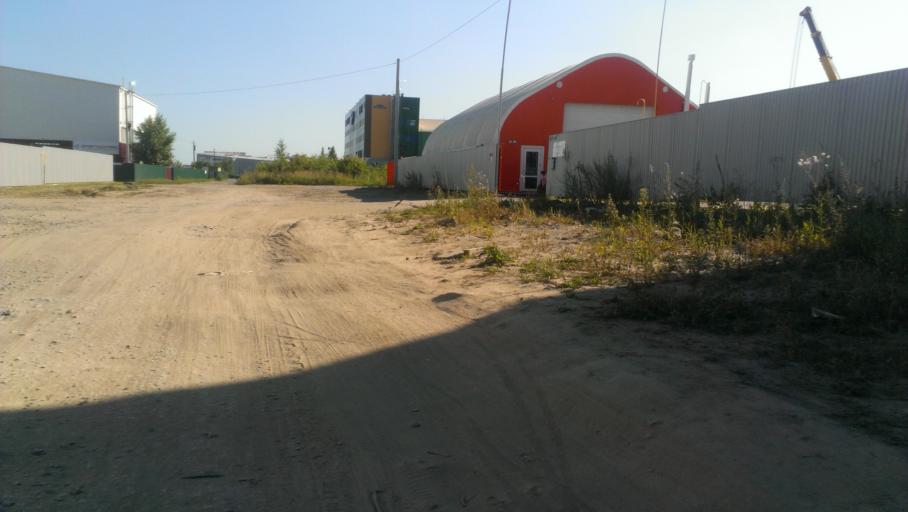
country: RU
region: Altai Krai
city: Novosilikatnyy
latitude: 53.3348
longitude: 83.6647
